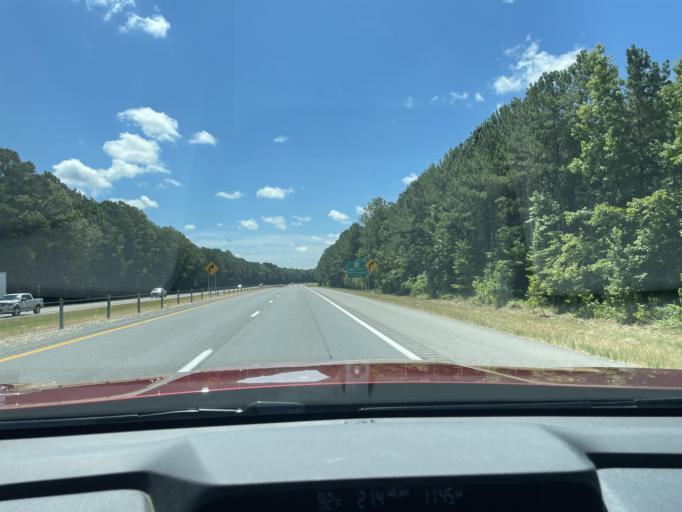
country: US
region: Arkansas
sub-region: Jefferson County
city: White Hall
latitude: 34.2962
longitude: -92.1271
